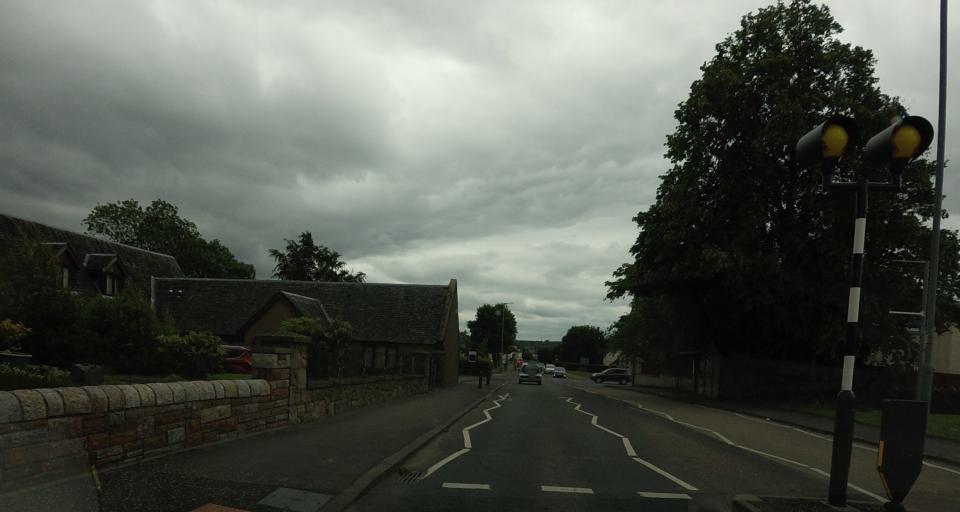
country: GB
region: Scotland
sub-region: Stirling
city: Bannockburn
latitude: 56.0925
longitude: -3.9331
